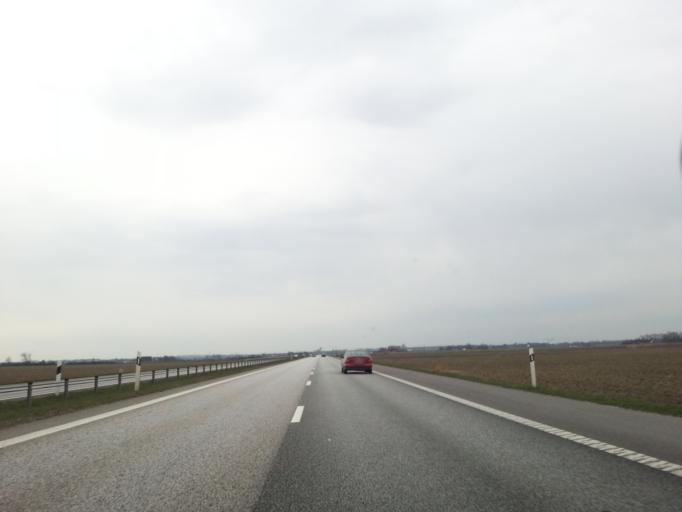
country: SE
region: Skane
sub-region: Angelholms Kommun
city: AEngelholm
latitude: 56.2975
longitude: 12.9050
